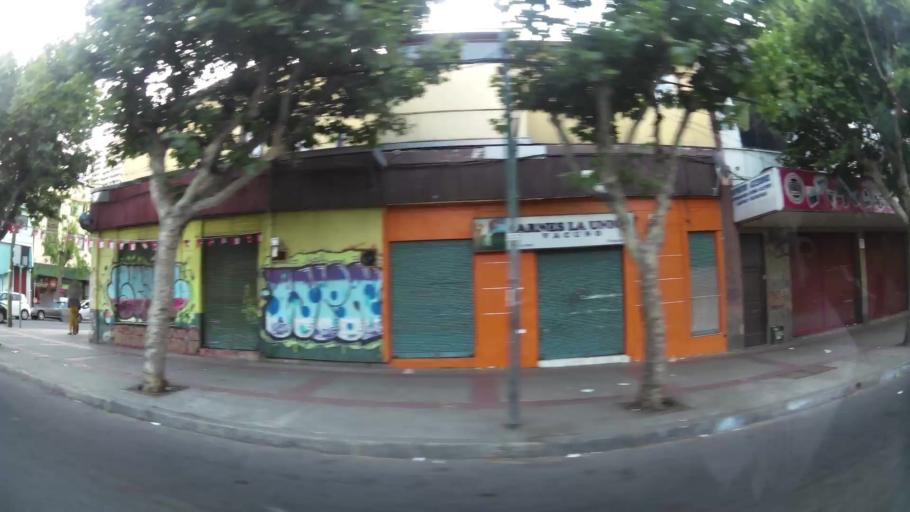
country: CL
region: Valparaiso
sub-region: Provincia de Valparaiso
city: Valparaiso
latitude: -33.0496
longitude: -71.6084
